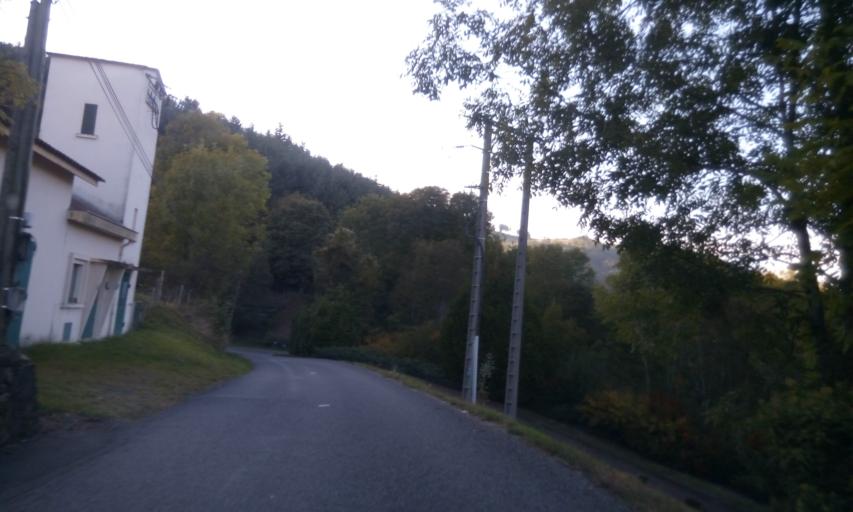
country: FR
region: Rhone-Alpes
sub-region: Departement du Rhone
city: Tarare
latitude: 45.9222
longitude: 4.4558
